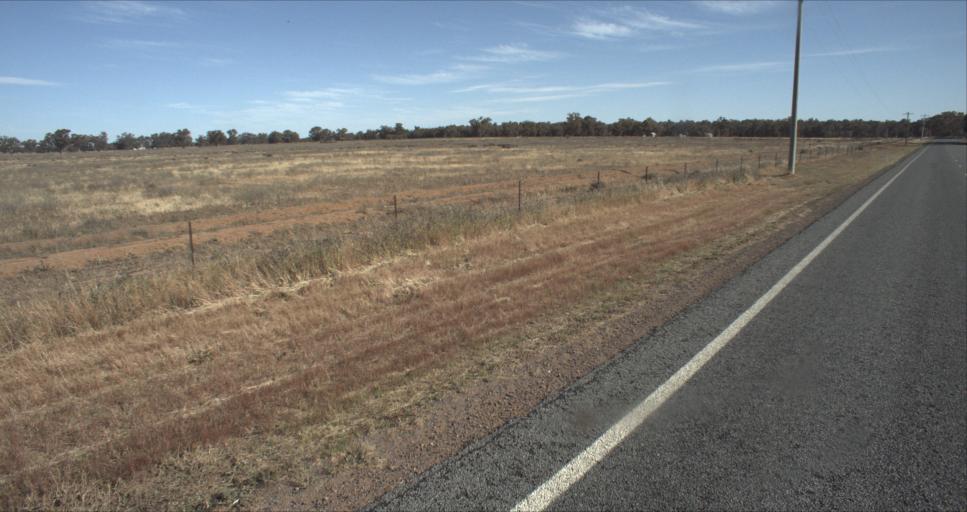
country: AU
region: New South Wales
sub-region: Leeton
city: Leeton
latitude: -34.6192
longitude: 146.3984
